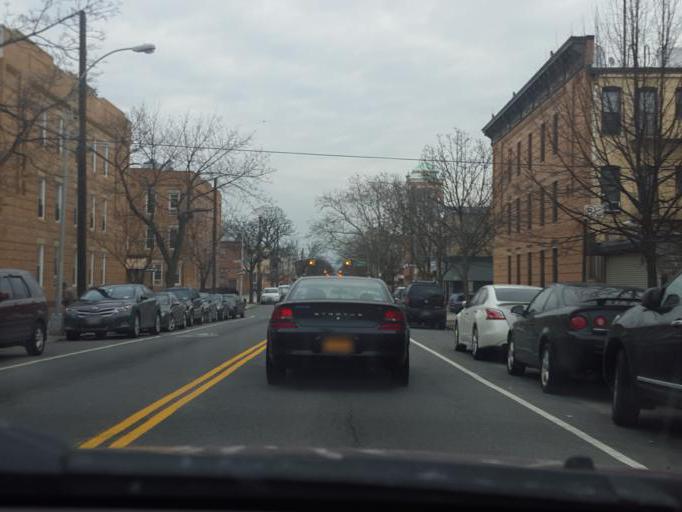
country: US
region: New York
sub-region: Kings County
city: East New York
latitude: 40.7026
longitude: -73.8895
